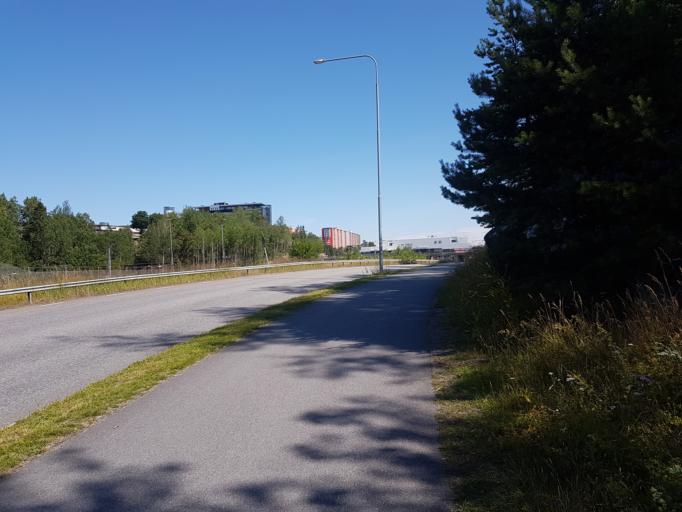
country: SE
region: Stockholm
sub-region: Huddinge Kommun
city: Huddinge
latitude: 59.2155
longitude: 17.9428
